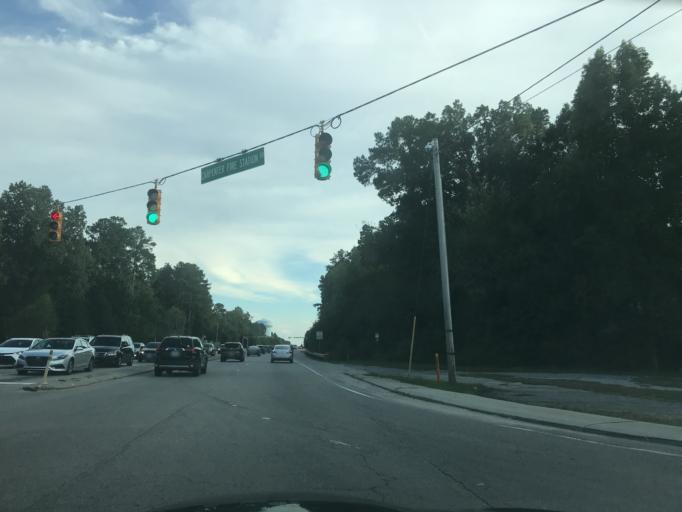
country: US
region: North Carolina
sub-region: Wake County
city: Morrisville
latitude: 35.8235
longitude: -78.8743
